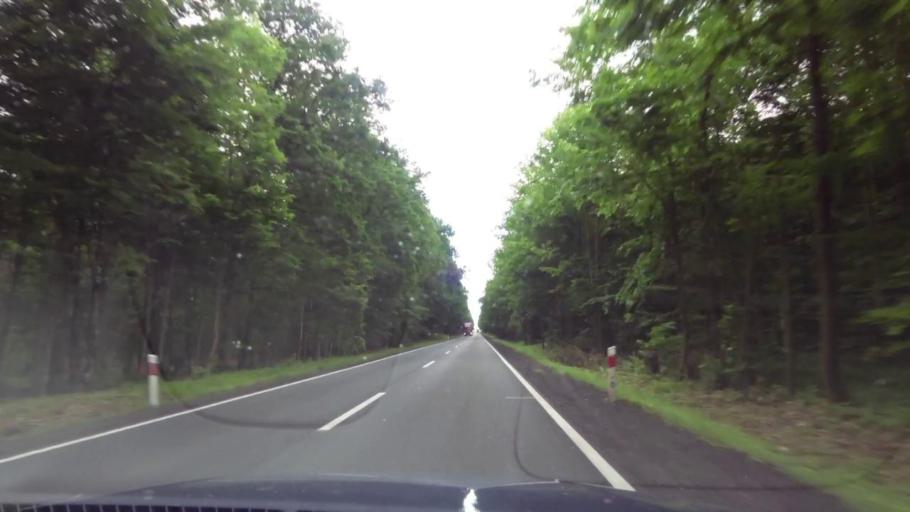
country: PL
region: West Pomeranian Voivodeship
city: Trzcinsko Zdroj
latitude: 52.9706
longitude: 14.7369
